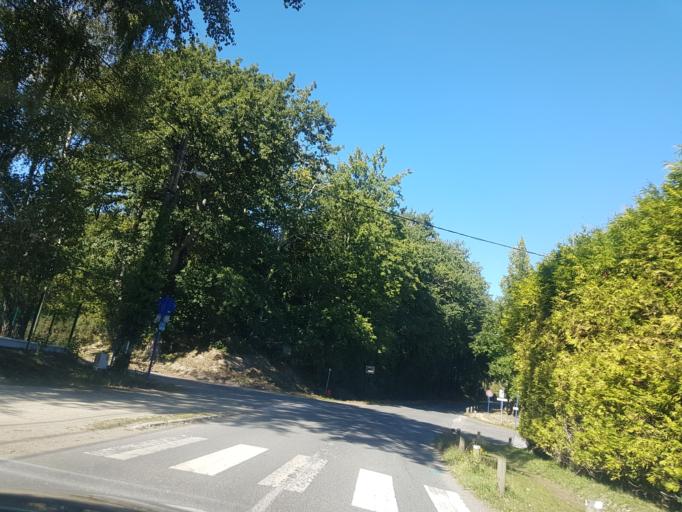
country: FR
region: Pays de la Loire
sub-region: Departement de la Loire-Atlantique
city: Mesquer
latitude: 47.3940
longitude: -2.4502
